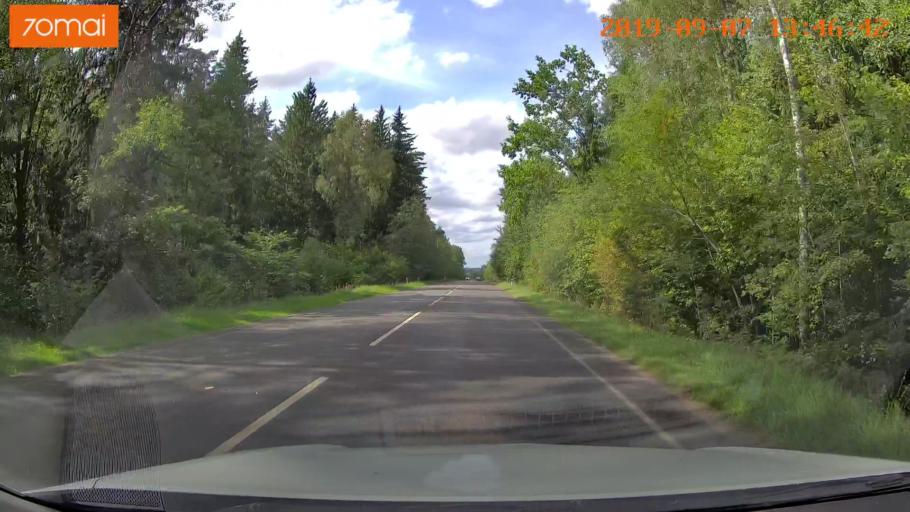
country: LT
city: Baltoji Voke
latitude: 54.5923
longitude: 25.2277
